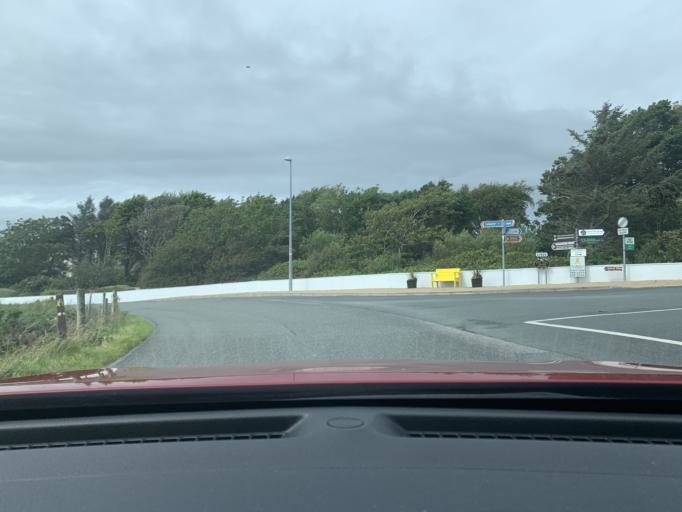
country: IE
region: Ulster
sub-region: County Donegal
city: Dungloe
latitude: 54.9529
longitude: -8.3707
